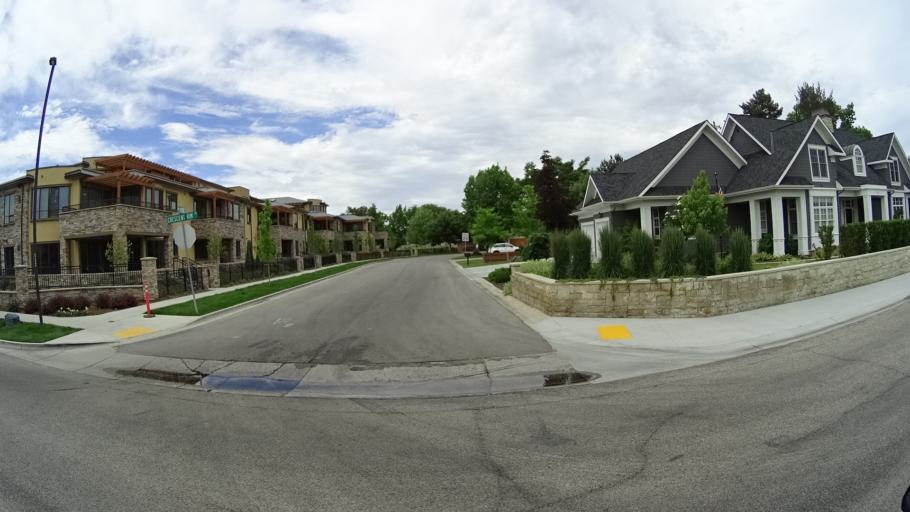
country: US
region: Idaho
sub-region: Ada County
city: Boise
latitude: 43.6051
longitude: -116.2196
